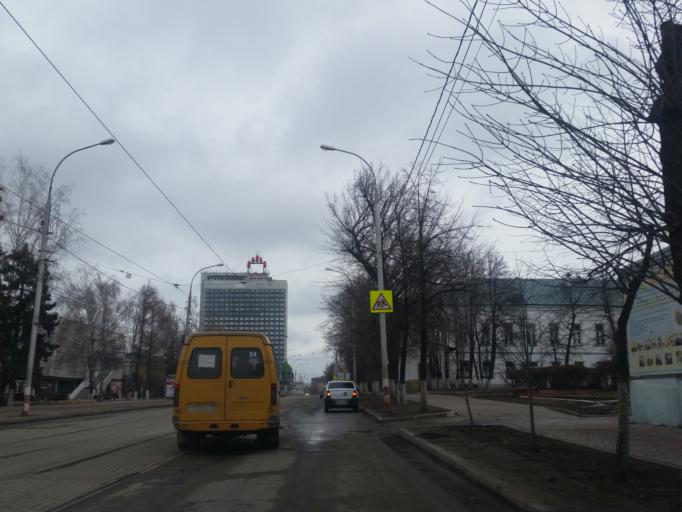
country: RU
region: Ulyanovsk
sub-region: Ulyanovskiy Rayon
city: Ulyanovsk
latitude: 54.3155
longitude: 48.4014
